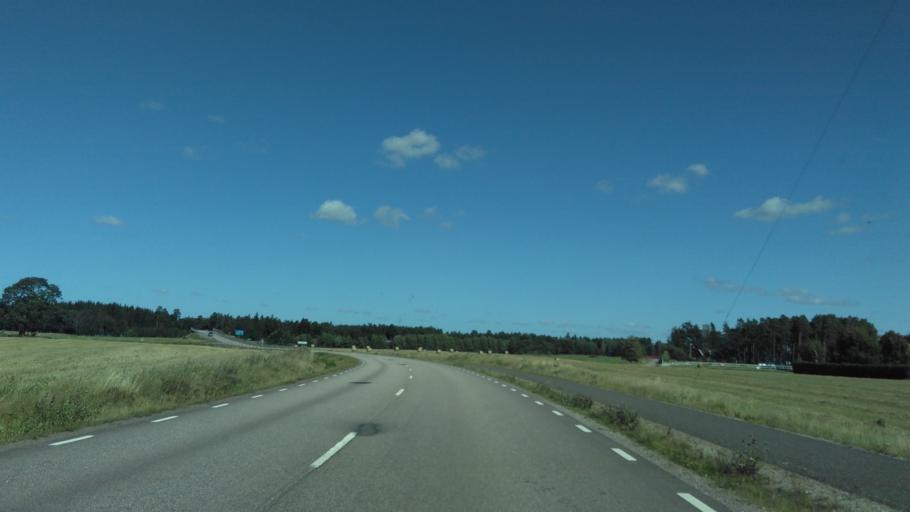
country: SE
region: Vaestra Goetaland
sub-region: Skara Kommun
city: Axvall
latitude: 58.3917
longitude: 13.5300
